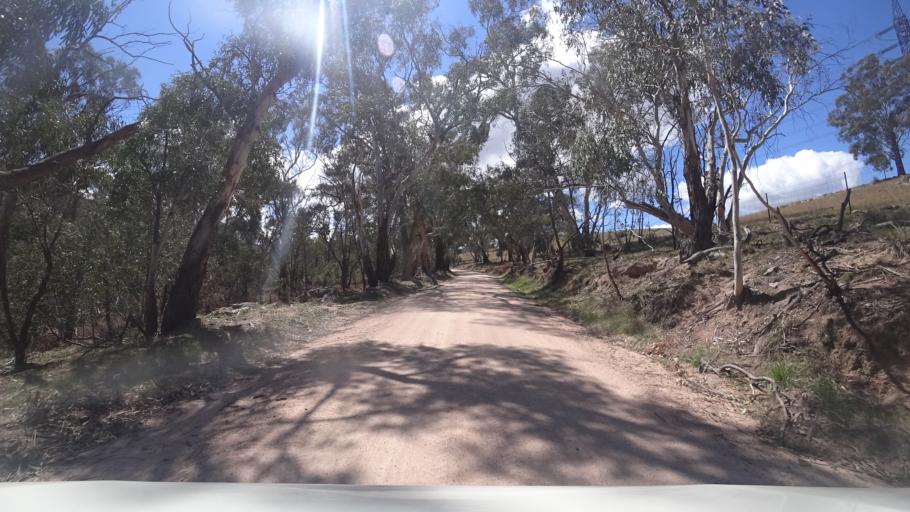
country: AU
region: New South Wales
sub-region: Oberon
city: Oberon
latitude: -33.5497
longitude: 149.9309
